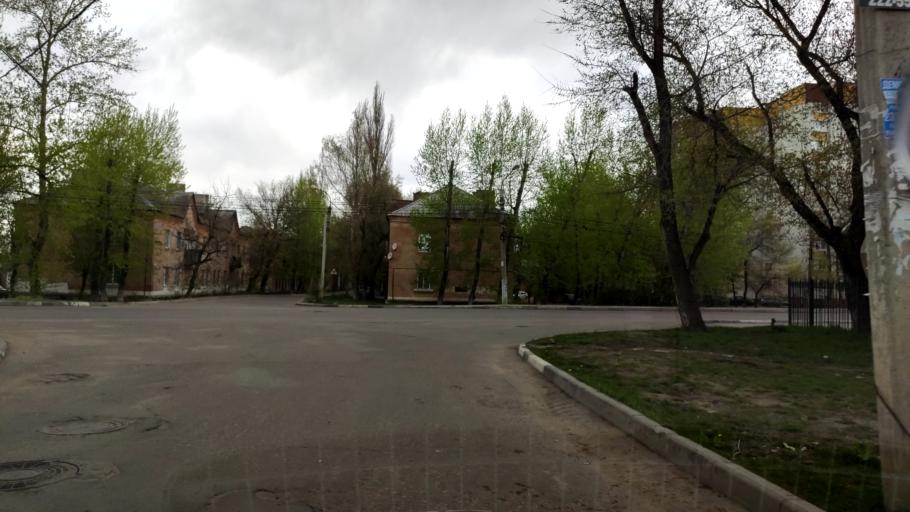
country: RU
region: Voronezj
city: Pridonskoy
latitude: 51.6825
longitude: 39.0769
